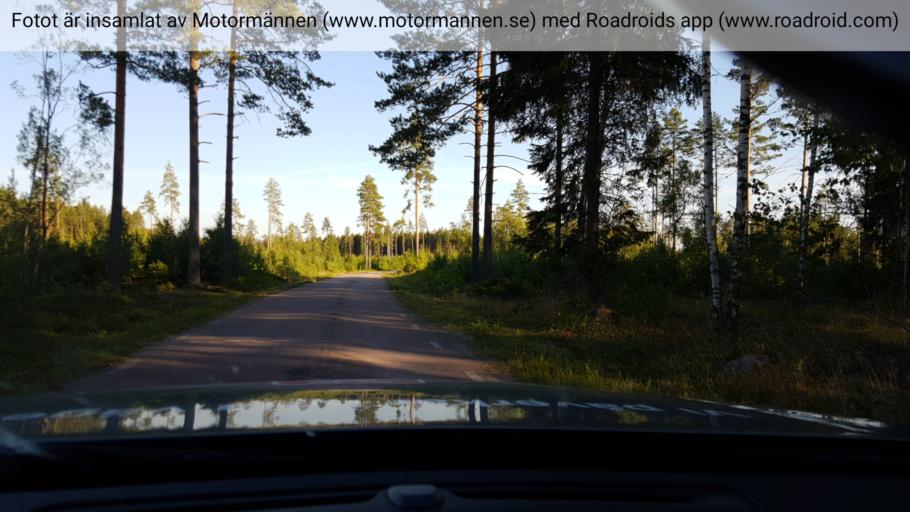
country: SE
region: Vaestmanland
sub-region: Surahammars Kommun
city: Surahammar
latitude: 59.6670
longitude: 16.0813
